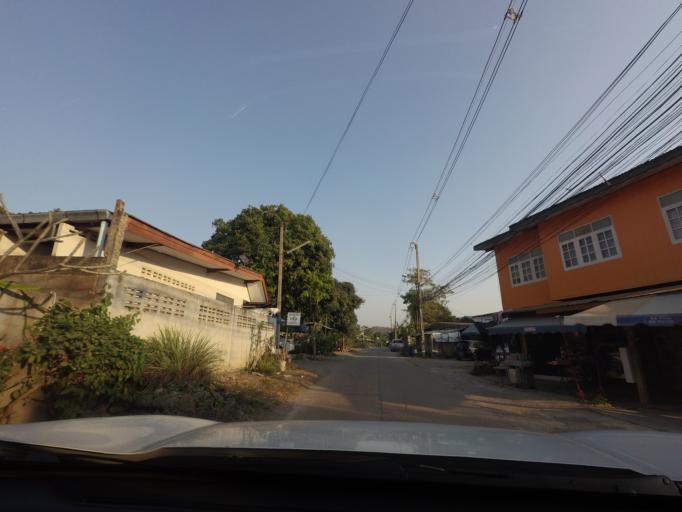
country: TH
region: Nakhon Ratchasima
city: Pak Chong
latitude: 14.6436
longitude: 101.3564
